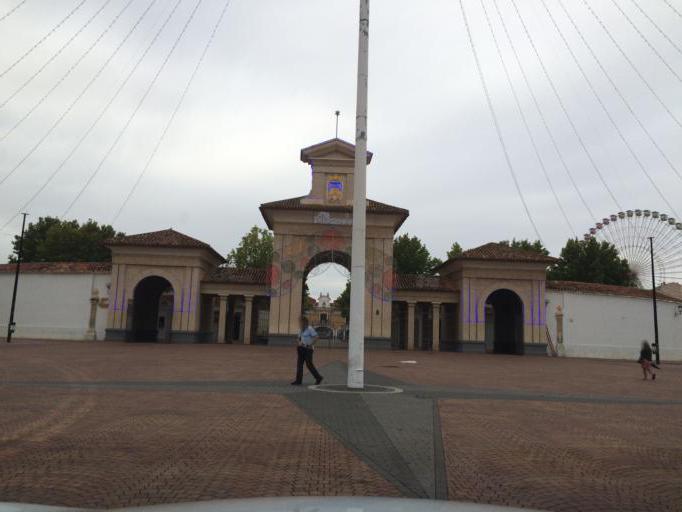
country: ES
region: Castille-La Mancha
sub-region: Provincia de Albacete
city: Albacete
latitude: 38.9969
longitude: -1.8677
